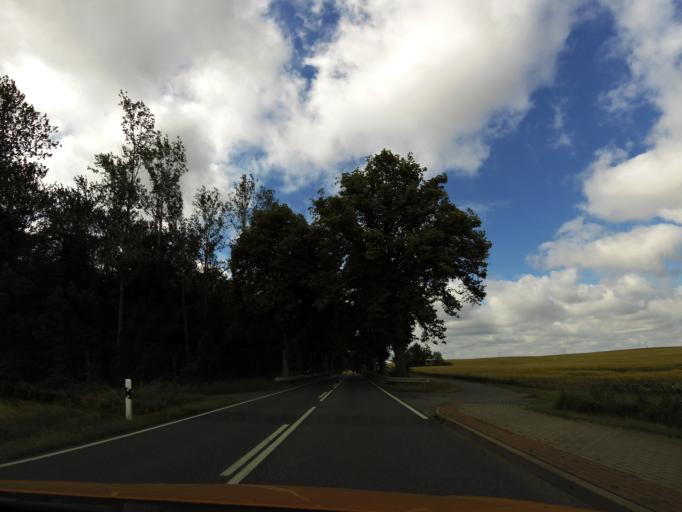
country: DE
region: Mecklenburg-Vorpommern
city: Krakow am See
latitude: 53.6947
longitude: 12.2727
